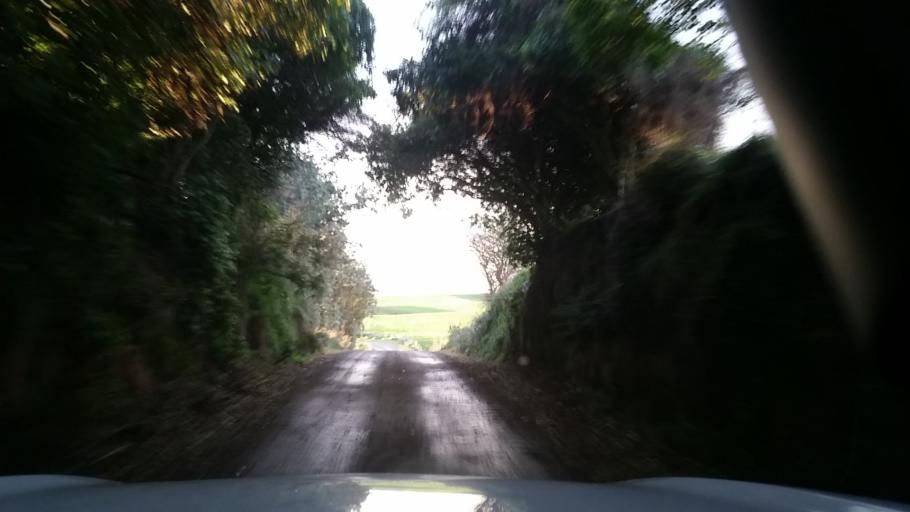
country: NZ
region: Manawatu-Wanganui
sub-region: Wanganui District
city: Wanganui
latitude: -39.8021
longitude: 174.8037
